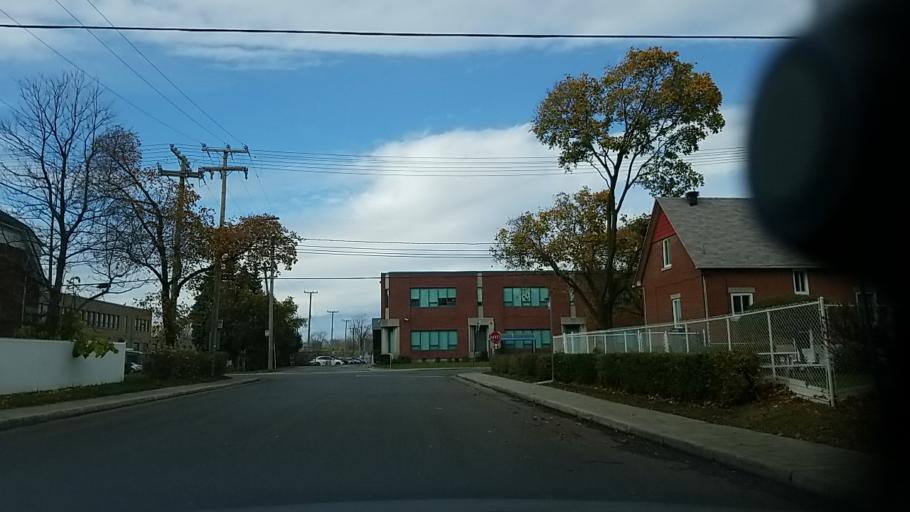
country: CA
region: Quebec
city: Saint-Laurent
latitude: 45.5135
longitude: -73.6642
